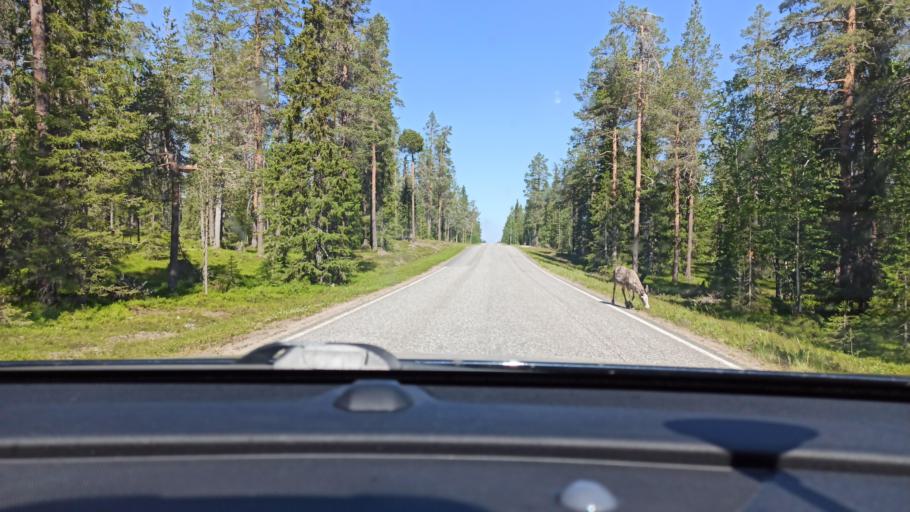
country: FI
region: Lapland
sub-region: Tunturi-Lappi
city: Kolari
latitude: 67.6721
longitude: 24.1484
